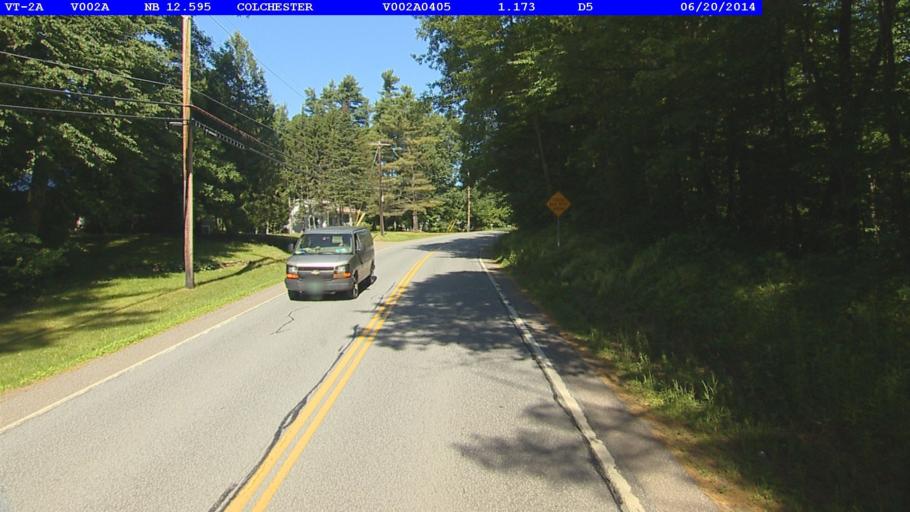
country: US
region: Vermont
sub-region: Chittenden County
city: Colchester
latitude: 44.5407
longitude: -73.1442
